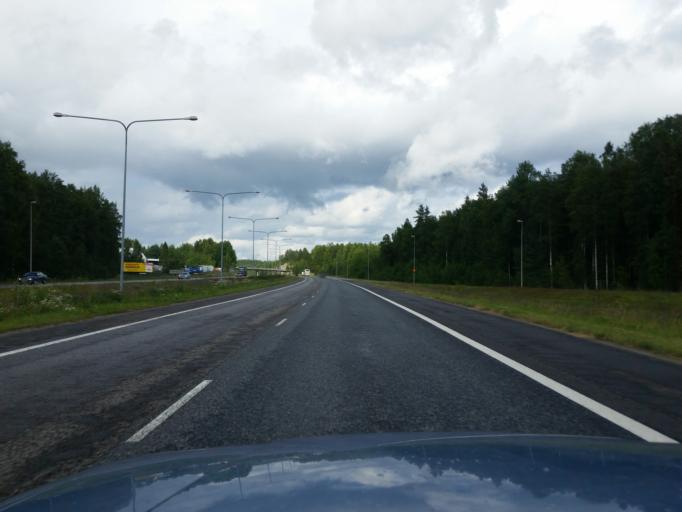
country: FI
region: Paijanne Tavastia
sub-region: Lahti
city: Heinola
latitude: 61.2358
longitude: 26.0445
